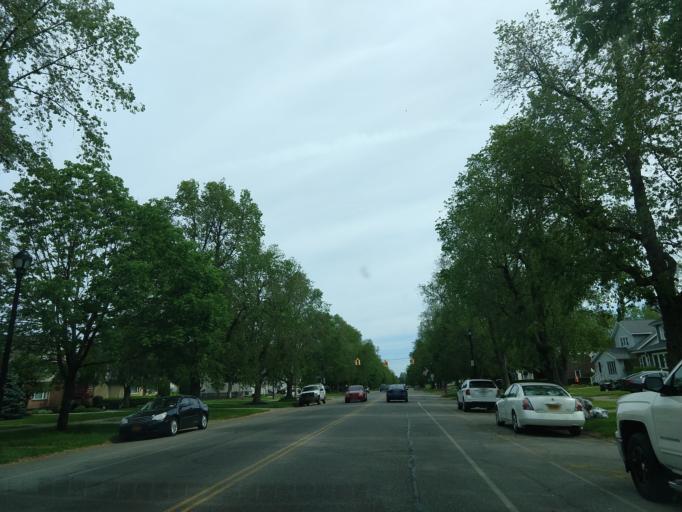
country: US
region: New York
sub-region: Erie County
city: Lackawanna
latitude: 42.8340
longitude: -78.8152
